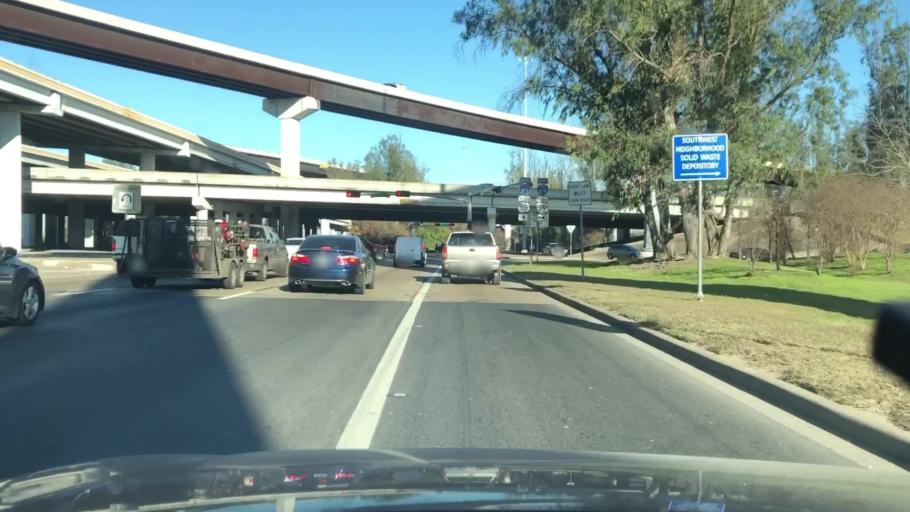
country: US
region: Texas
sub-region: Fort Bend County
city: Meadows Place
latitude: 29.6605
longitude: -95.5568
